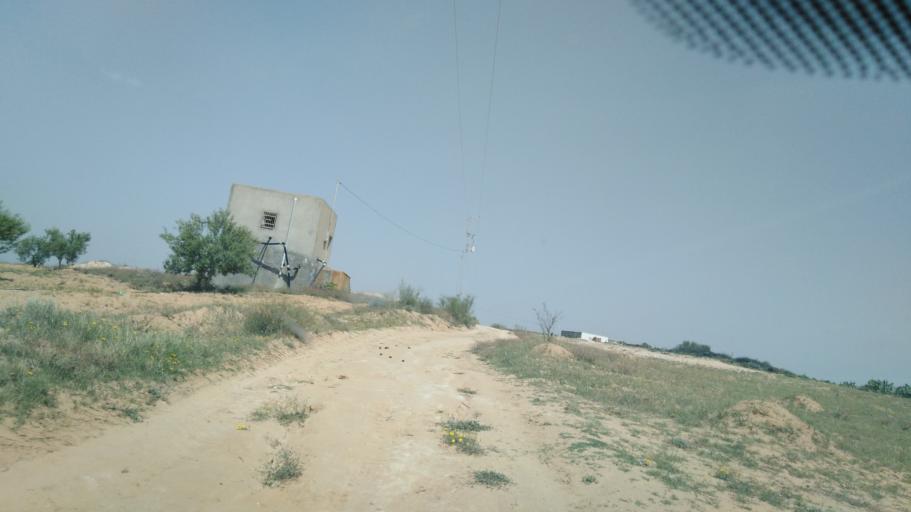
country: TN
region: Safaqis
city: Sfax
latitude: 34.7450
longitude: 10.5695
